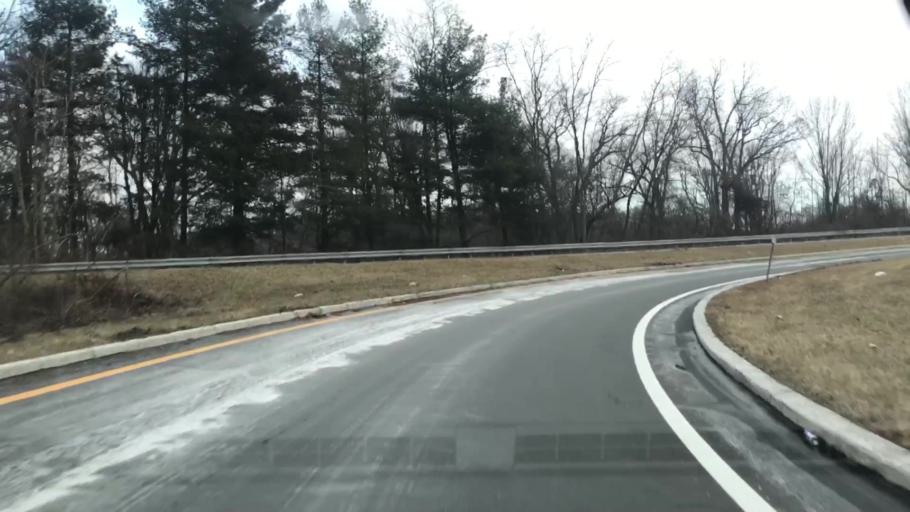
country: US
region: New Jersey
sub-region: Essex County
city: Roseland
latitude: 40.8078
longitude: -74.2873
